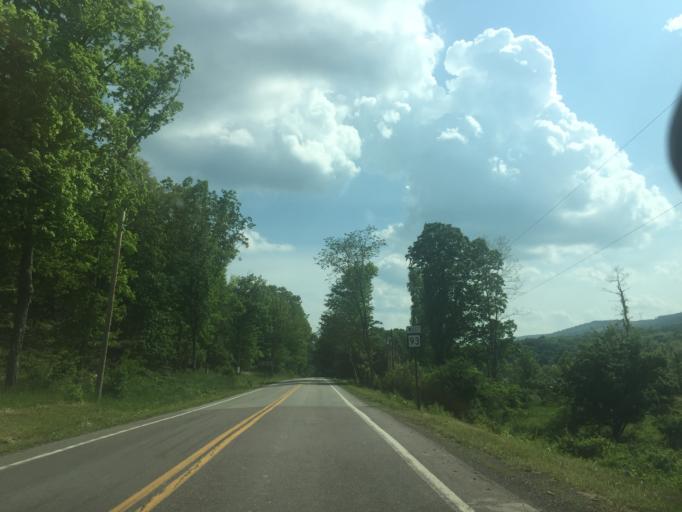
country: US
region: West Virginia
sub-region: Grant County
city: Petersburg
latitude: 39.2198
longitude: -79.1588
